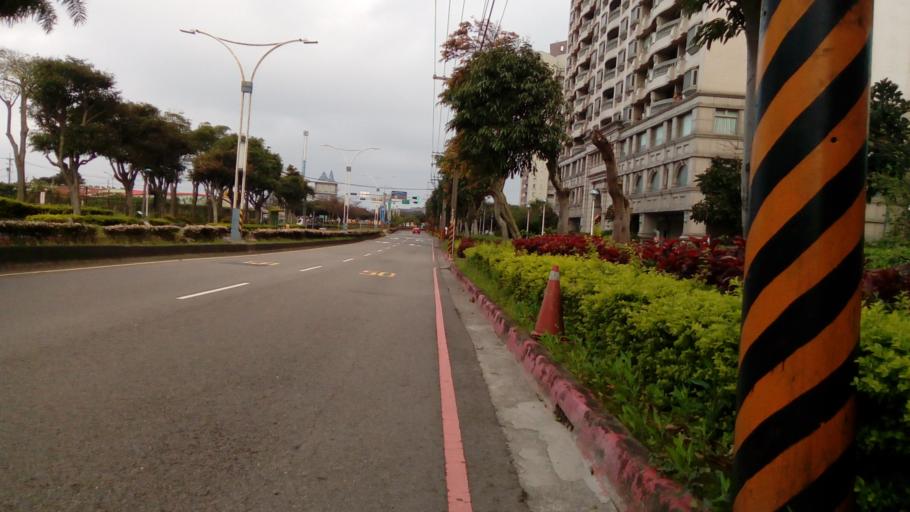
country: TW
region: Taipei
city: Taipei
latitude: 25.1786
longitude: 121.4231
